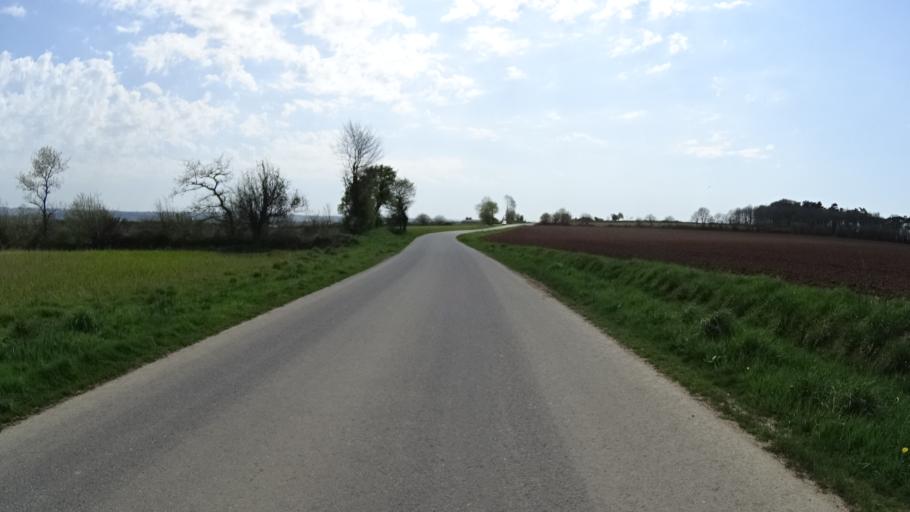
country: FR
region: Brittany
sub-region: Departement du Finistere
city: Sizun
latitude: 48.4407
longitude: -4.1153
